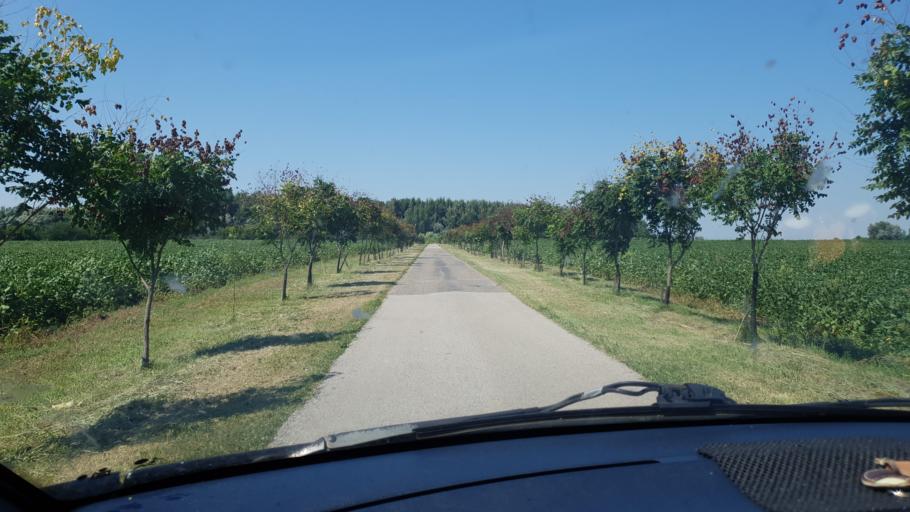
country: RS
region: Autonomna Pokrajina Vojvodina
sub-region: Juznobacki Okrug
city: Kovilj
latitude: 45.1987
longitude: 20.0647
